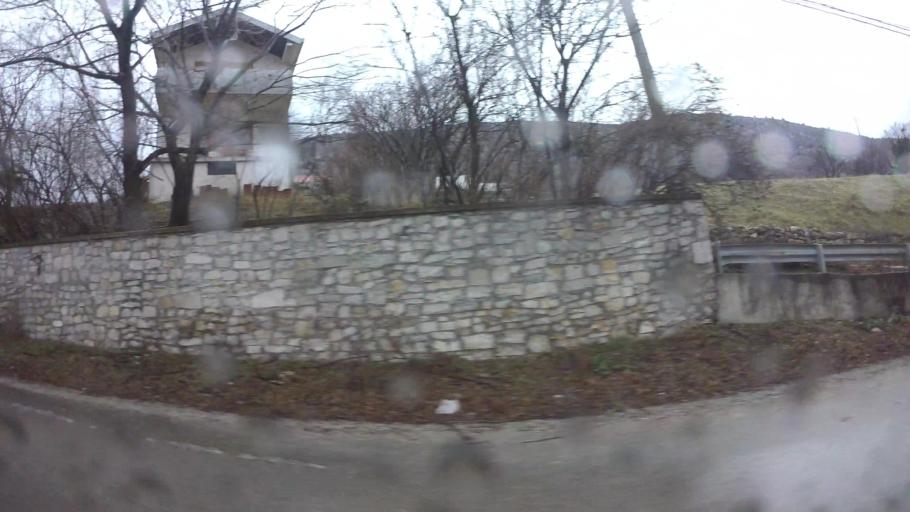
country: BA
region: Federation of Bosnia and Herzegovina
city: Blagaj
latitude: 43.2948
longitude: 17.8571
